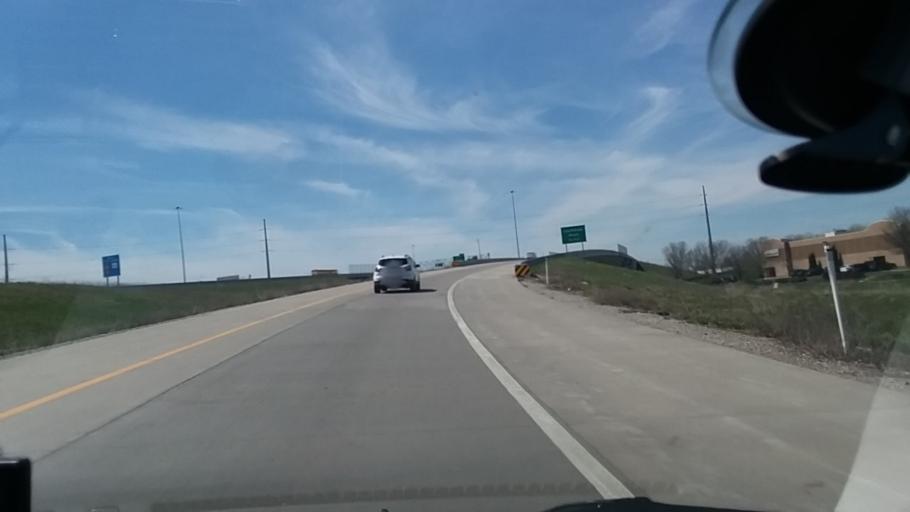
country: US
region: Kansas
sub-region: Johnson County
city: Lenexa
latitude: 38.9414
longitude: -94.7488
